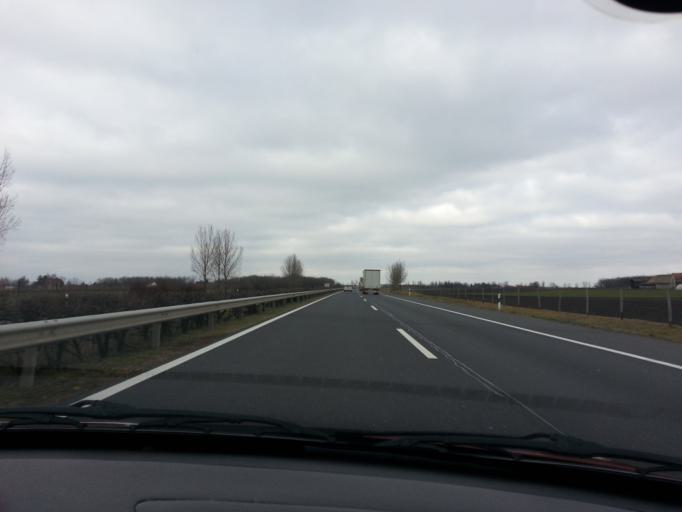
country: HU
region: Bacs-Kiskun
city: Kiskunfelegyhaza
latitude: 46.6945
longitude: 19.8084
